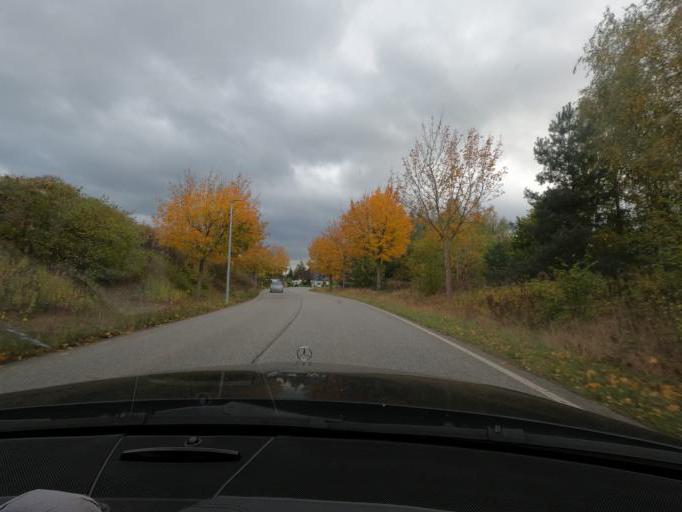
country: DE
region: Schleswig-Holstein
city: Geesthacht
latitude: 53.4510
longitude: 10.3679
